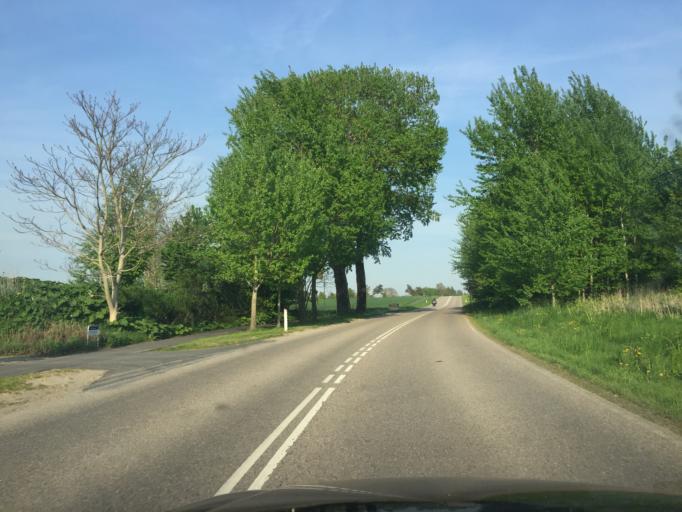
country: DK
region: Capital Region
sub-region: Hoje-Taastrup Kommune
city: Flong
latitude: 55.6791
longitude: 12.2275
